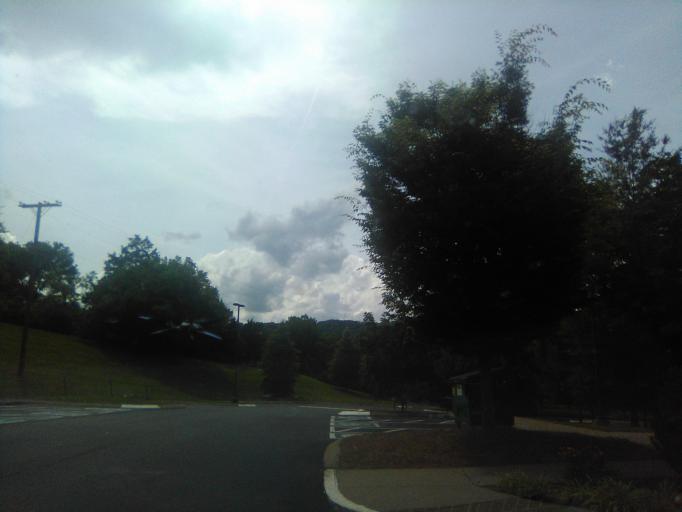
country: US
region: Tennessee
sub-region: Davidson County
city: Belle Meade
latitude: 36.0903
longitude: -86.8876
